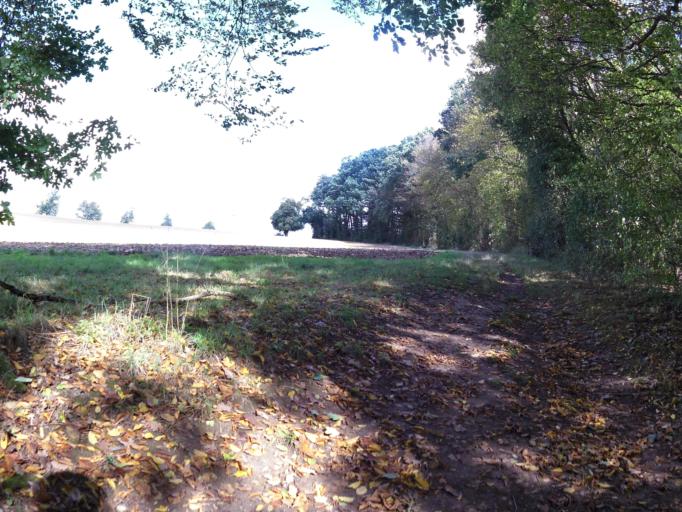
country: DE
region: Bavaria
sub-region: Regierungsbezirk Unterfranken
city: Margetshochheim
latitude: 49.8305
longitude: 9.8381
